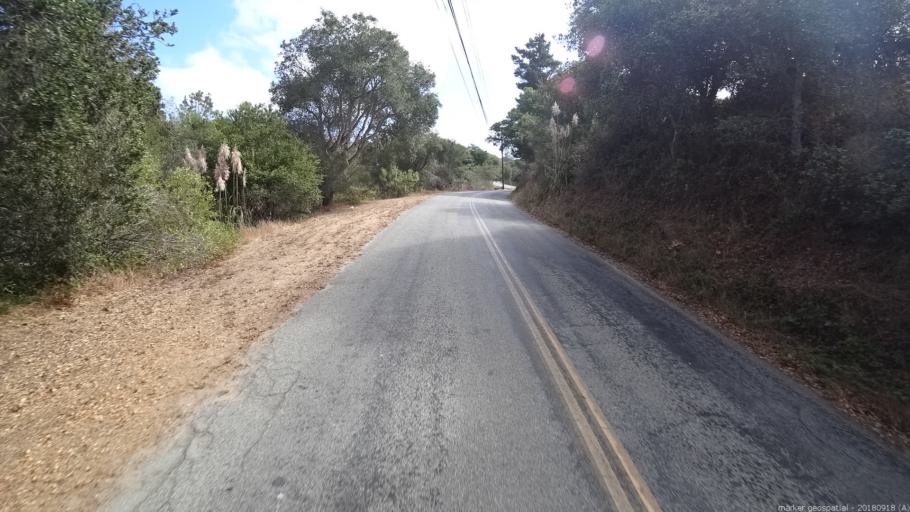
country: US
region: California
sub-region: Monterey County
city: Prunedale
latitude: 36.8019
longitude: -121.6321
